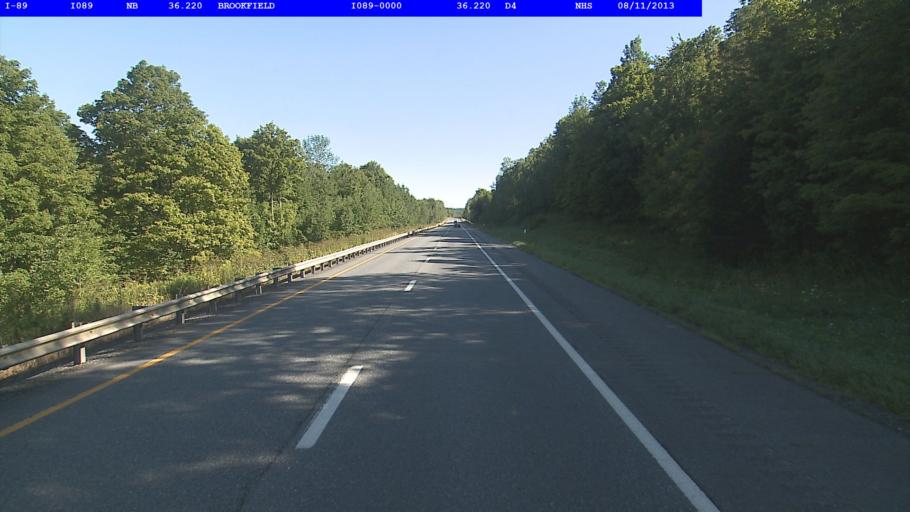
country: US
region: Vermont
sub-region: Orange County
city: Randolph
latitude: 44.0207
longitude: -72.6166
